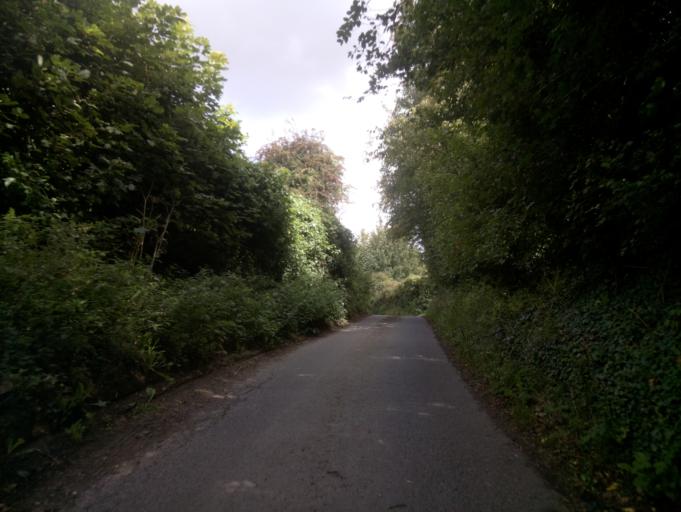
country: GB
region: England
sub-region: Wiltshire
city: Colerne
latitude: 51.4364
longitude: -2.2610
